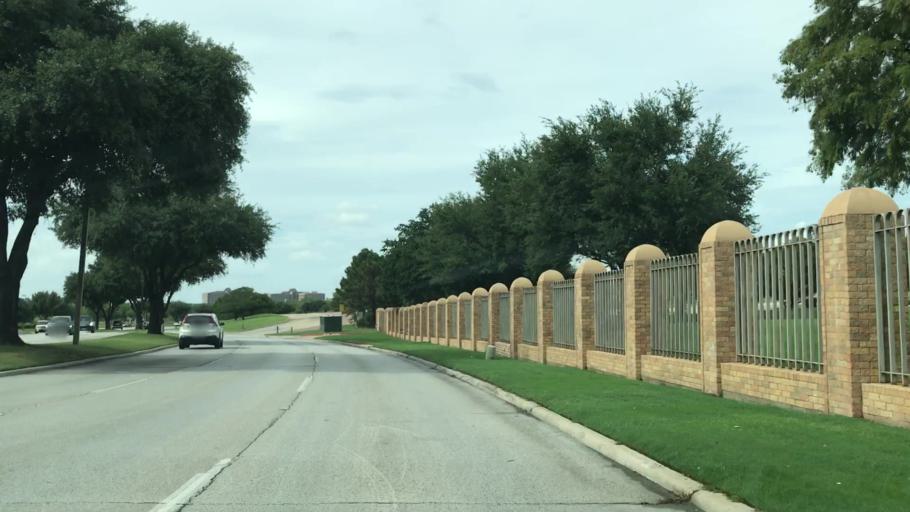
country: US
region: Texas
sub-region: Dallas County
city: Irving
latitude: 32.8652
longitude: -96.9596
